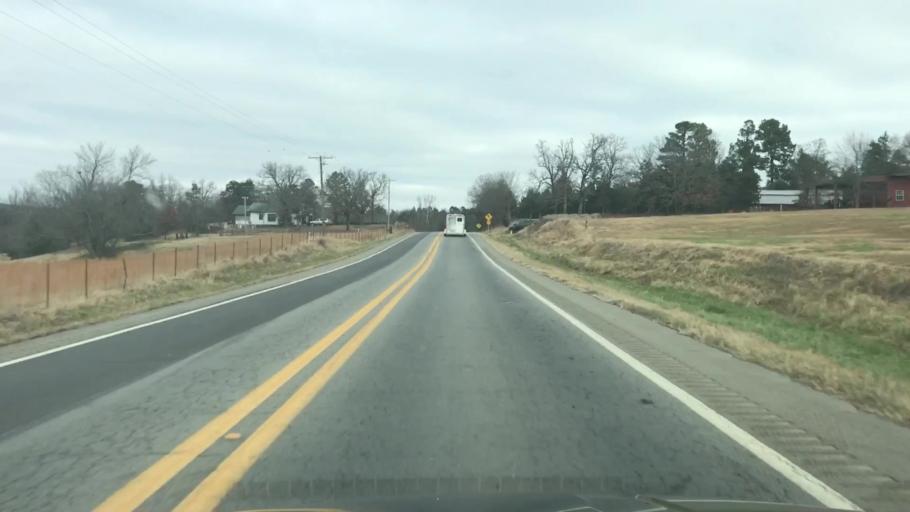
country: US
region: Arkansas
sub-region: Scott County
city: Waldron
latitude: 34.9486
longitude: -94.1047
